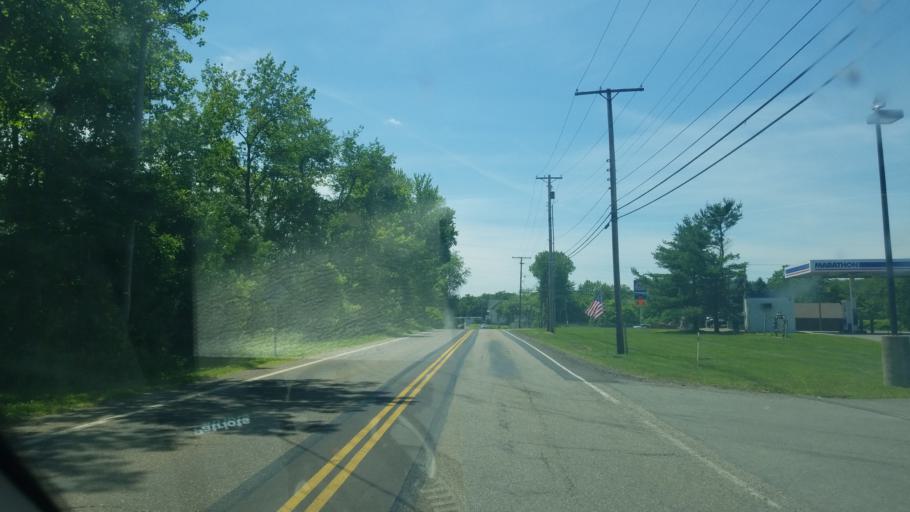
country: US
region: Ohio
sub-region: Stark County
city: East Canton
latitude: 40.8267
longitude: -81.3059
